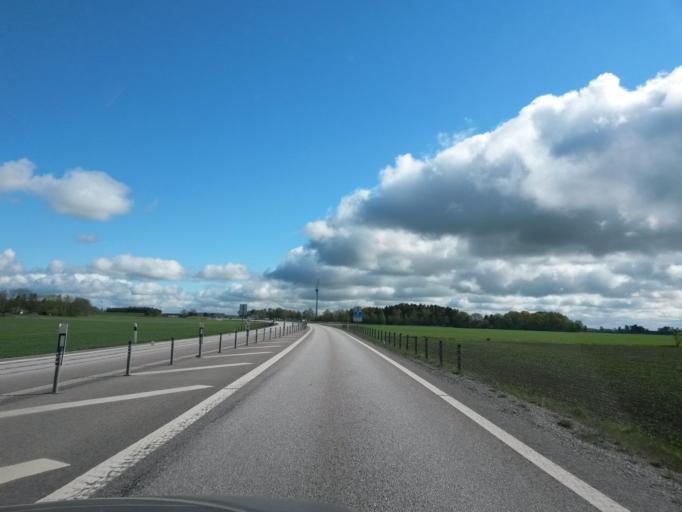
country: SE
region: Vaestra Goetaland
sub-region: Vara Kommun
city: Vara
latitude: 58.2711
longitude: 13.0101
